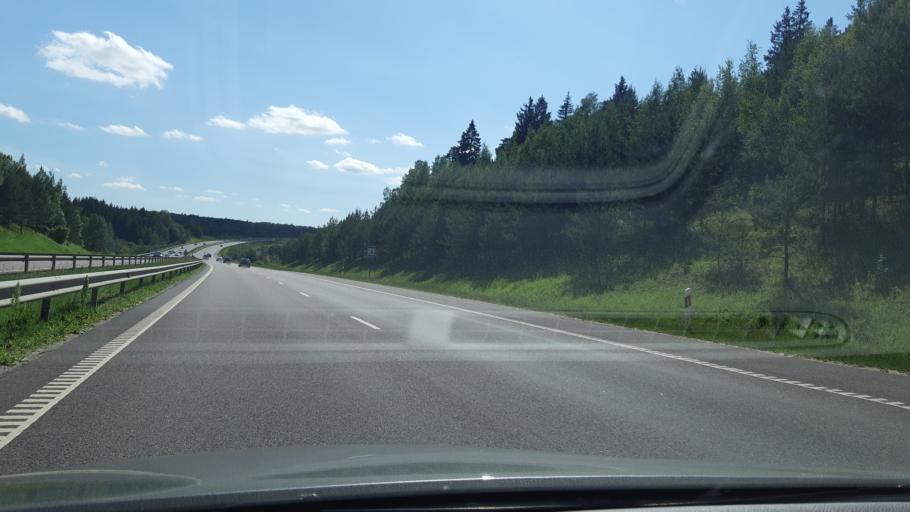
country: LT
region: Kauno apskritis
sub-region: Kauno rajonas
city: Karmelava
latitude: 54.9890
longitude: 24.1107
